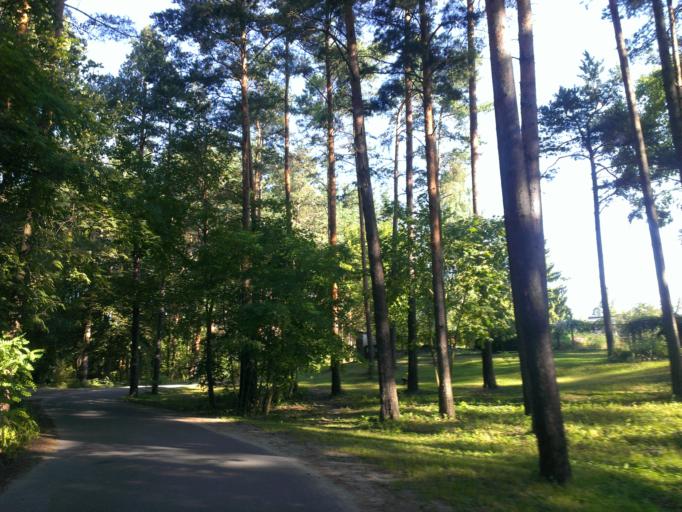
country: LV
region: Riga
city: Bergi
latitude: 56.9853
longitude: 24.3032
